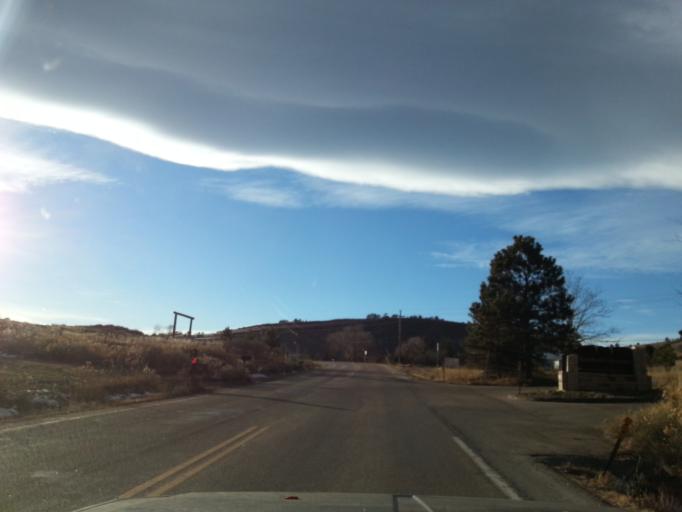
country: US
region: Colorado
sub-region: Larimer County
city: Laporte
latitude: 40.5224
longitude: -105.1813
